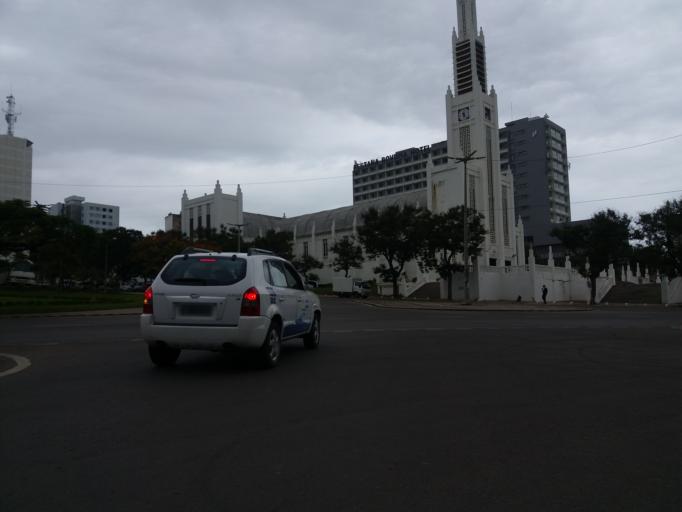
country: MZ
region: Maputo City
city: Maputo
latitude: -25.9690
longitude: 32.5733
